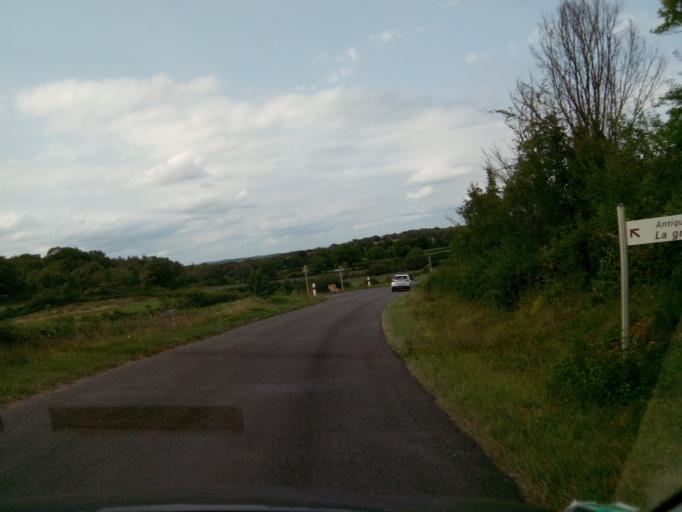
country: FR
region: Midi-Pyrenees
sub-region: Departement du Lot
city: Gramat
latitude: 44.8637
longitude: 1.7413
